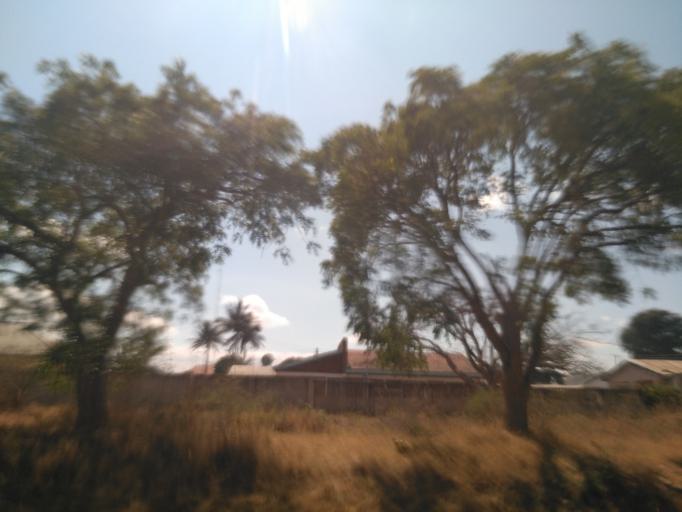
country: TZ
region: Dodoma
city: Dodoma
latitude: -6.1612
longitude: 35.7540
